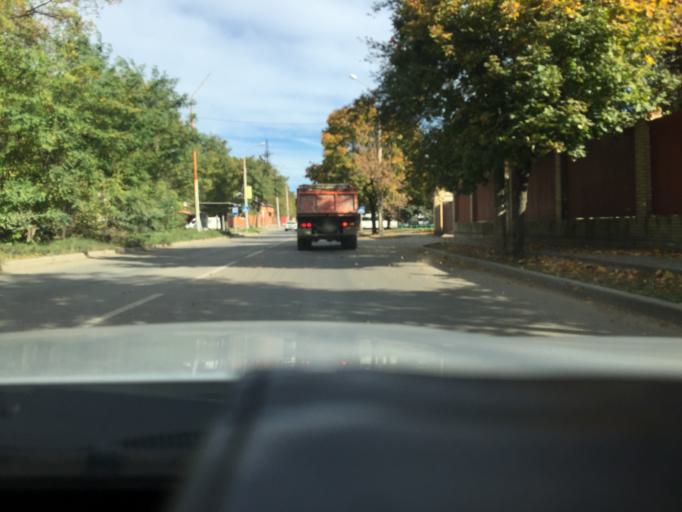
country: RU
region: Rostov
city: Imeni Chkalova
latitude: 47.2878
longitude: 39.8029
